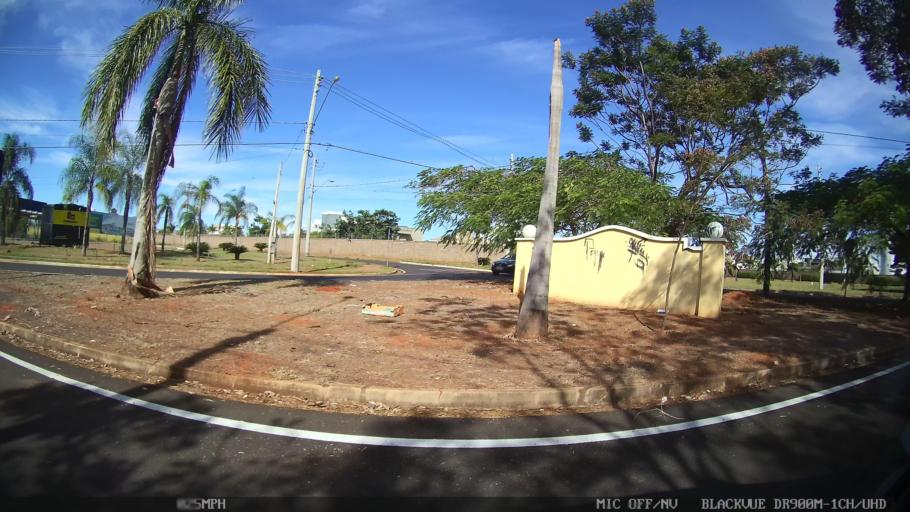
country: BR
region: Sao Paulo
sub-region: Sao Jose Do Rio Preto
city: Sao Jose do Rio Preto
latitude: -20.8062
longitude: -49.3320
